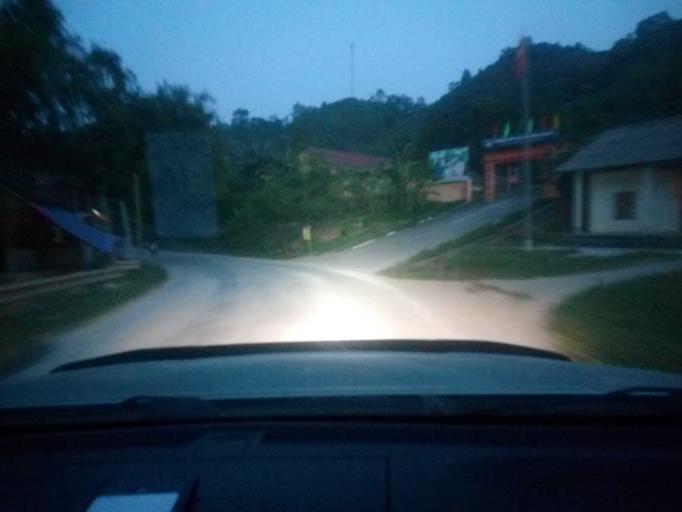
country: VN
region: Yen Bai
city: Co Phuc
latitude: 21.8782
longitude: 104.6680
